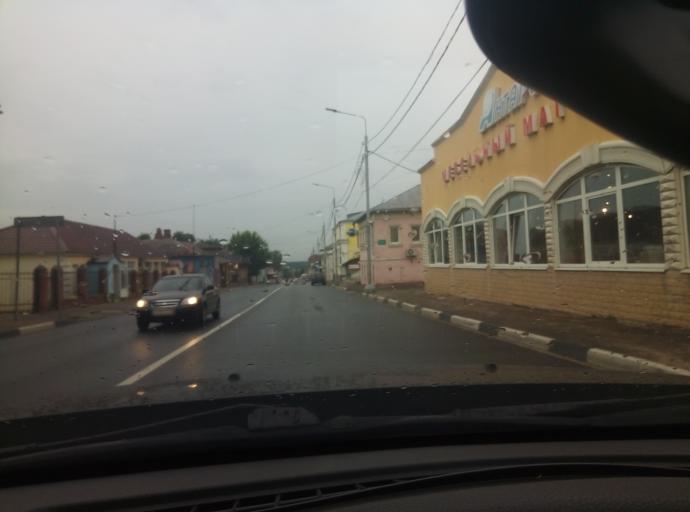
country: RU
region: Moskovskaya
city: Serpukhov
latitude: 54.9167
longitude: 37.4199
